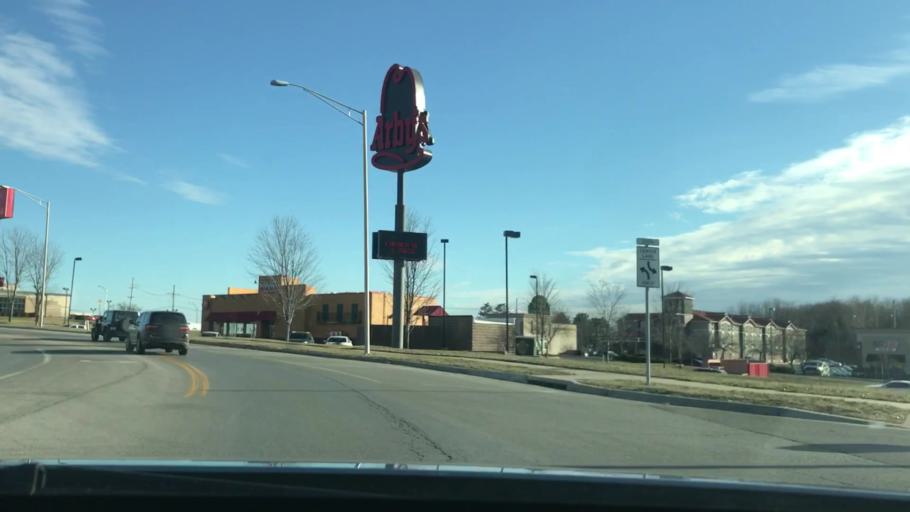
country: US
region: Missouri
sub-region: Platte County
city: Weatherby Lake
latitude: 39.2455
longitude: -94.6614
